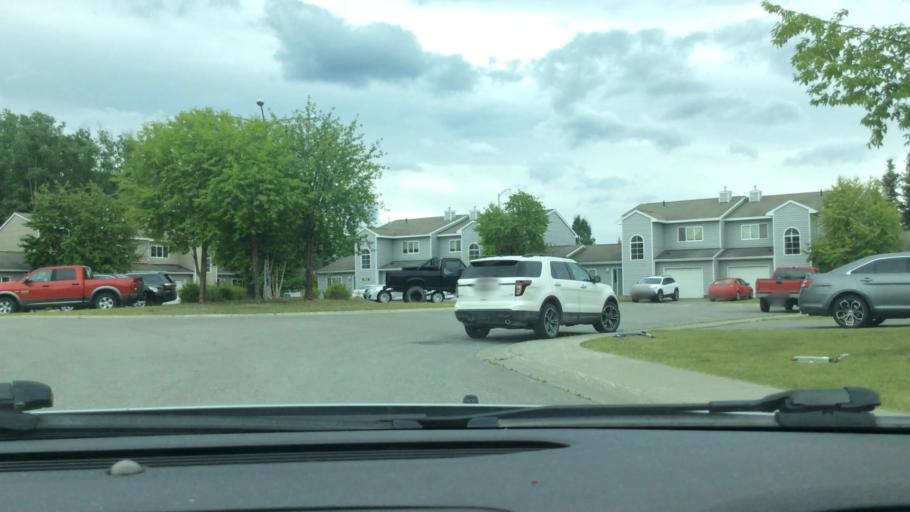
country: US
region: Alaska
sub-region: Anchorage Municipality
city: Anchorage
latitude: 61.2340
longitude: -149.7704
